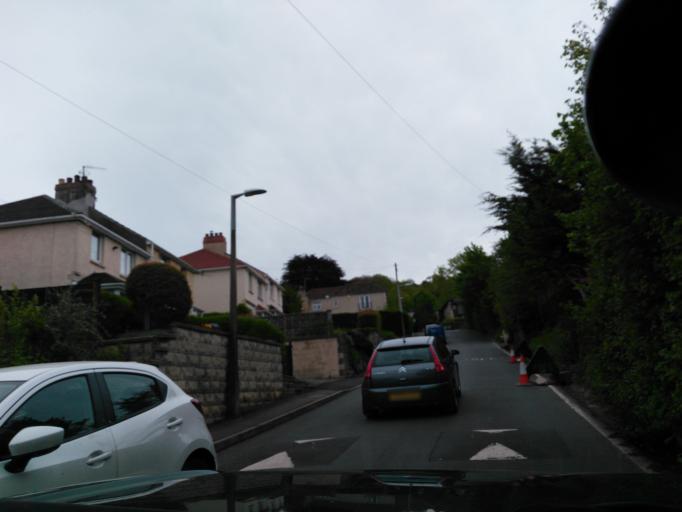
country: GB
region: England
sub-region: Bath and North East Somerset
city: Bath
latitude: 51.3929
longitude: -2.3242
